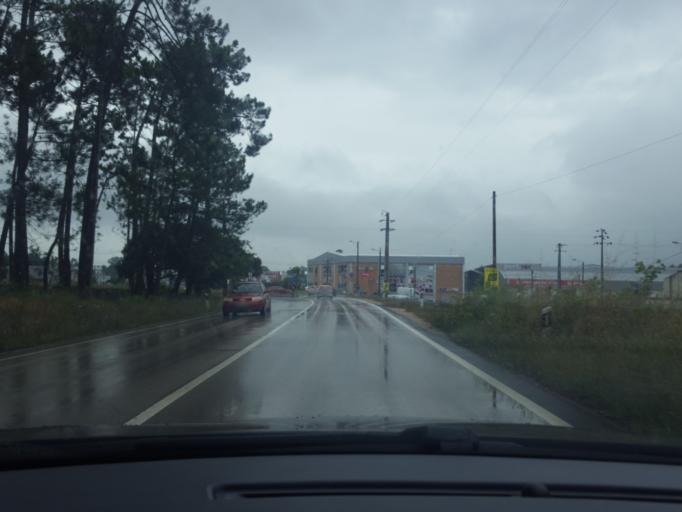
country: PT
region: Leiria
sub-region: Leiria
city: Leiria
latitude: 39.7340
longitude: -8.7623
